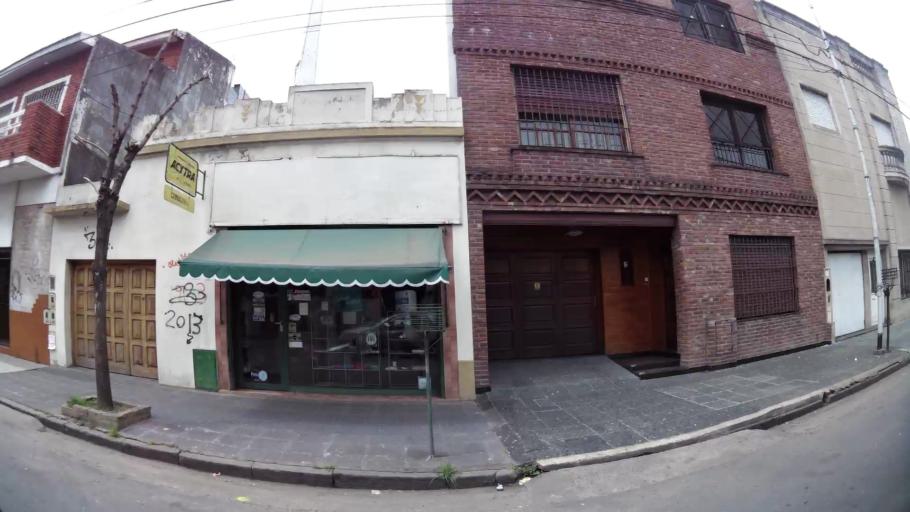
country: AR
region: Buenos Aires
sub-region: Partido de Avellaneda
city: Avellaneda
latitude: -34.6671
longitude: -58.3701
